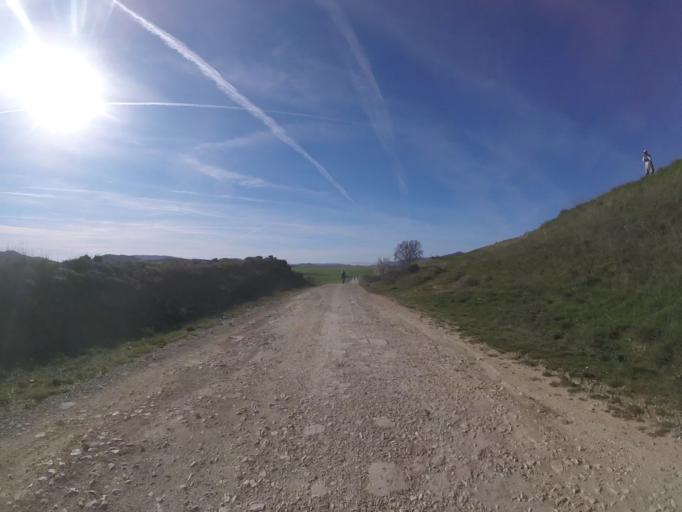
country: ES
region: Navarre
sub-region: Provincia de Navarra
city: Yerri
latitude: 42.7185
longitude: -1.9695
